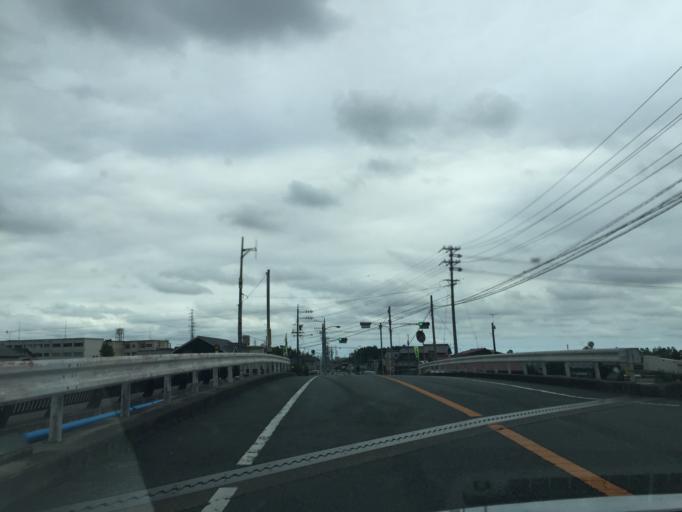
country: JP
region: Shizuoka
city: Fukuroi
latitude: 34.7687
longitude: 137.9132
